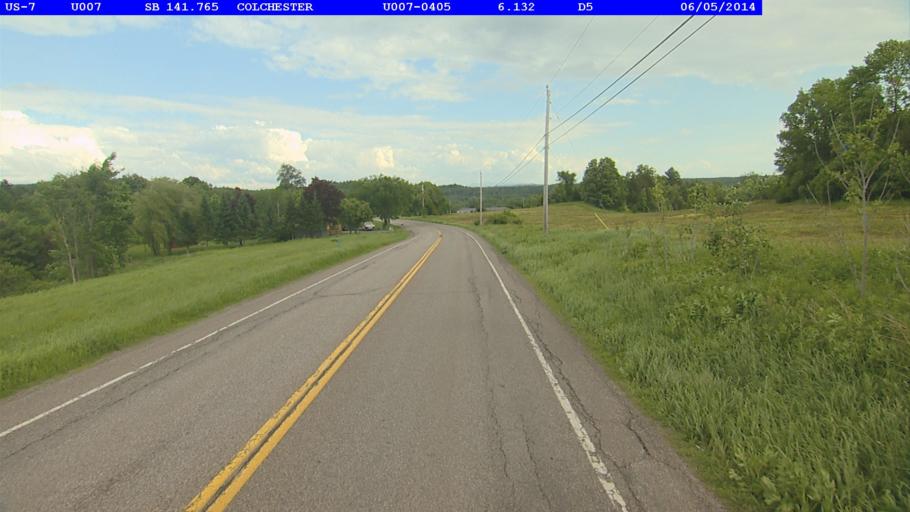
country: US
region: Vermont
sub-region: Chittenden County
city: Colchester
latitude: 44.5842
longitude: -73.1651
